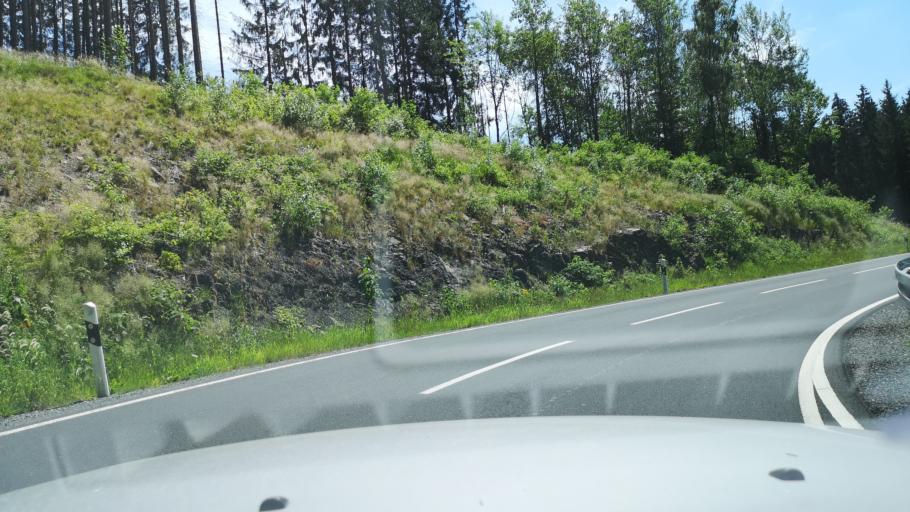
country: DE
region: Bavaria
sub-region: Upper Franconia
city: Teuschnitz
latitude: 50.3943
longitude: 11.3545
